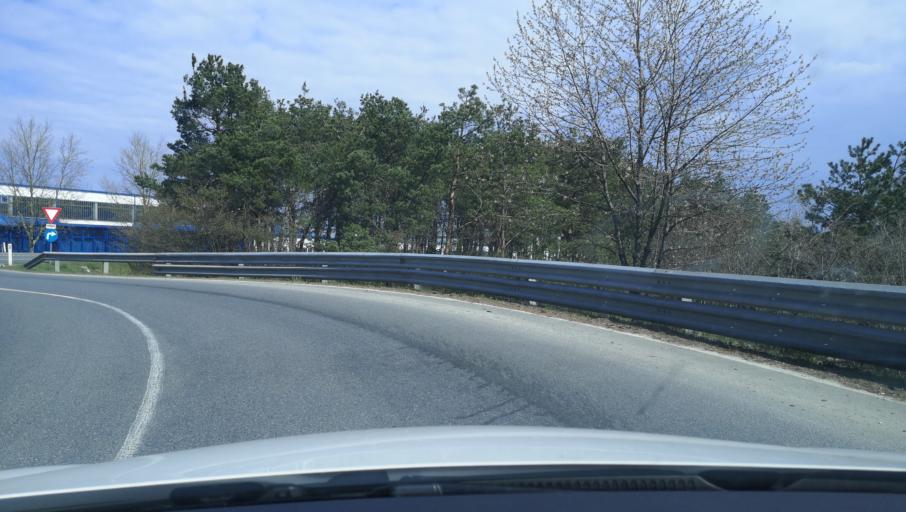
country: AT
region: Lower Austria
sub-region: Politischer Bezirk Amstetten
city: Winklarn
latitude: 48.1024
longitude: 14.8260
